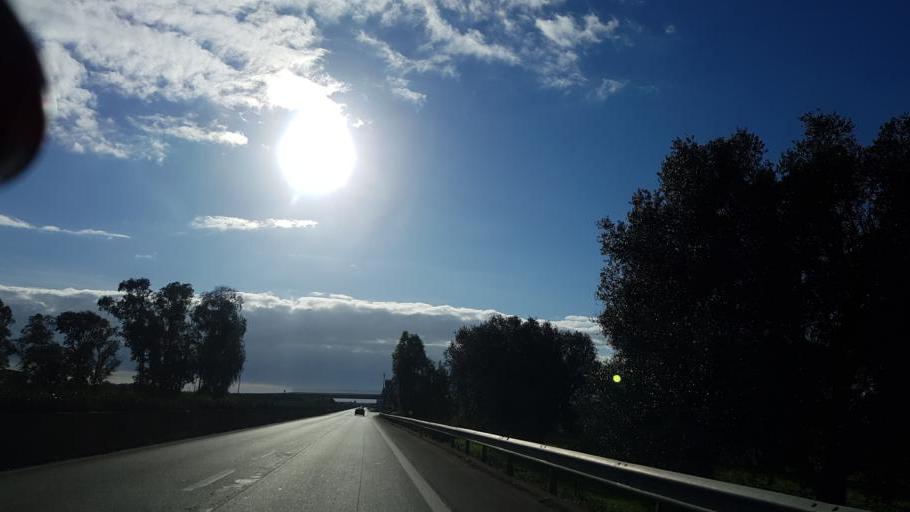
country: IT
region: Apulia
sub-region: Provincia di Brindisi
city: Tuturano
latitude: 40.5573
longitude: 17.9919
